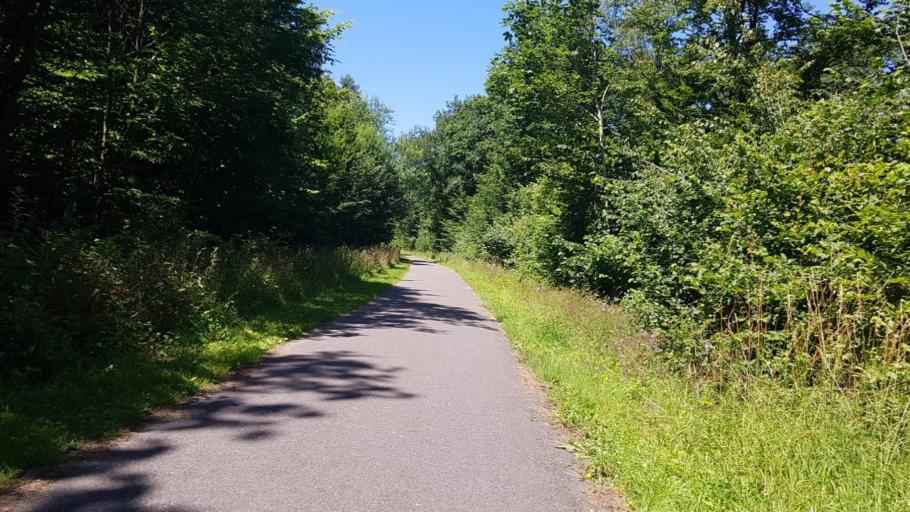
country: BE
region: Wallonia
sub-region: Province du Hainaut
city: Froidchapelle
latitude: 50.1542
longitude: 4.2703
